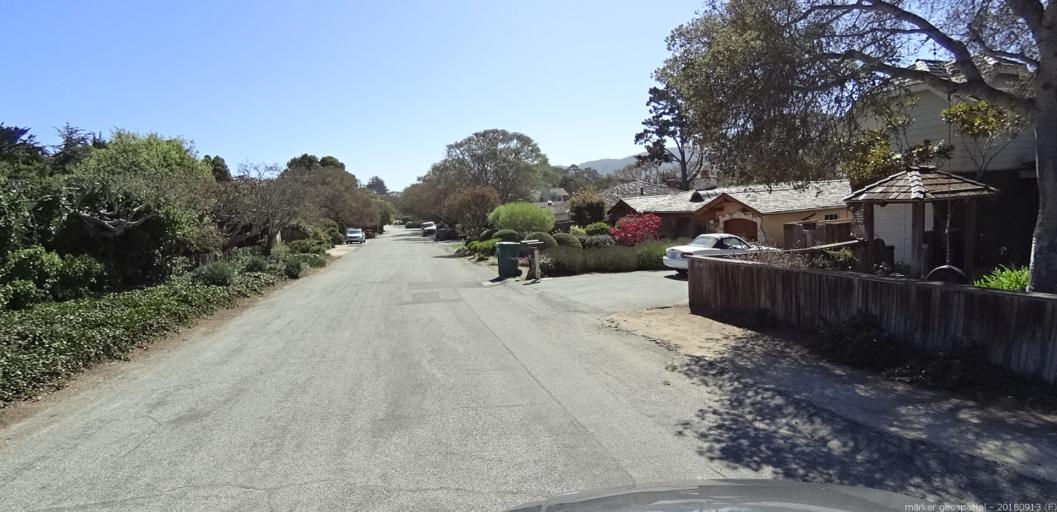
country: US
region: California
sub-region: Monterey County
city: Carmel-by-the-Sea
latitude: 36.5442
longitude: -121.9263
